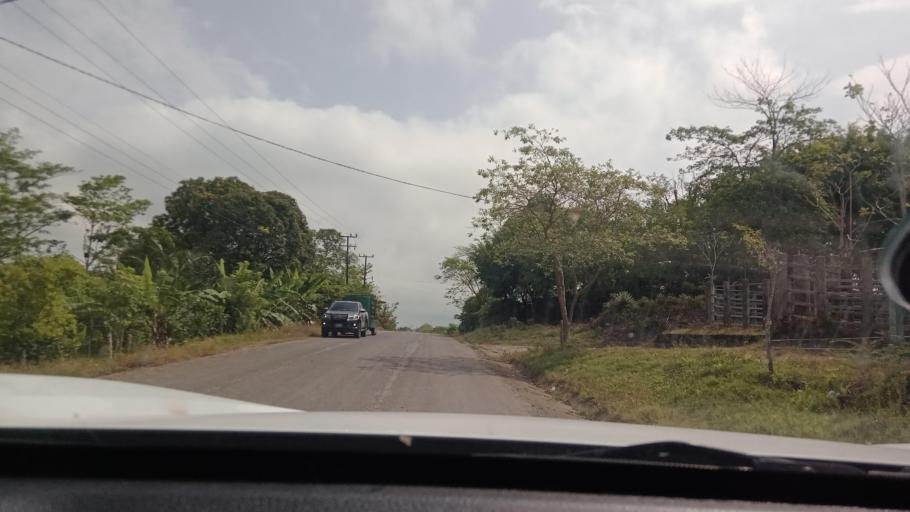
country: MX
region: Tabasco
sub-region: Huimanguillo
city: Francisco Rueda
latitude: 17.5683
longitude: -94.1116
